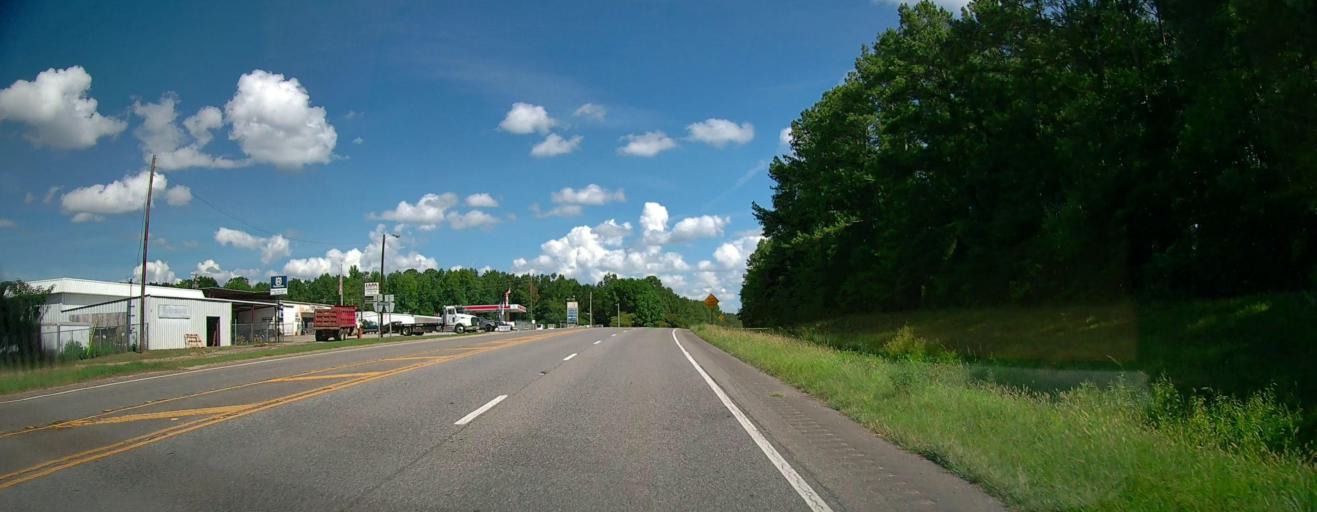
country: US
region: Alabama
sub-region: Pickens County
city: Gordo
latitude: 33.3125
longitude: -87.8929
